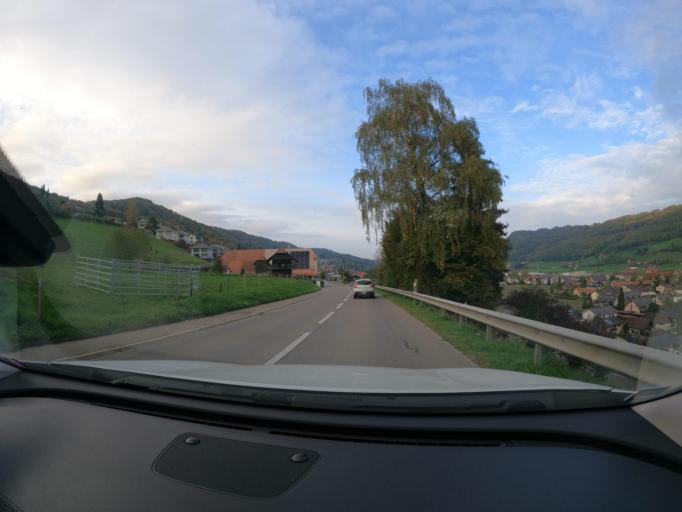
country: CH
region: Bern
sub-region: Bern-Mittelland District
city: Toffen
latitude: 46.8560
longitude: 7.4916
